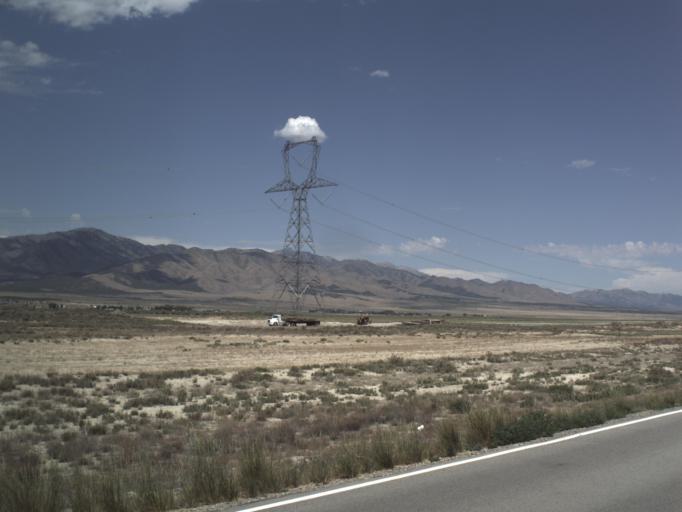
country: US
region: Utah
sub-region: Tooele County
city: Tooele
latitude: 40.3165
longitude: -112.4056
